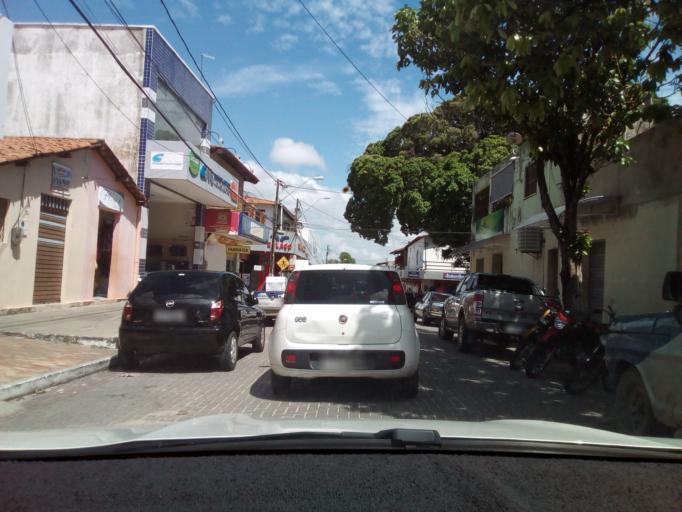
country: BR
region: Ceara
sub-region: Beberibe
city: Beberibe
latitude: -4.1821
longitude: -38.1295
